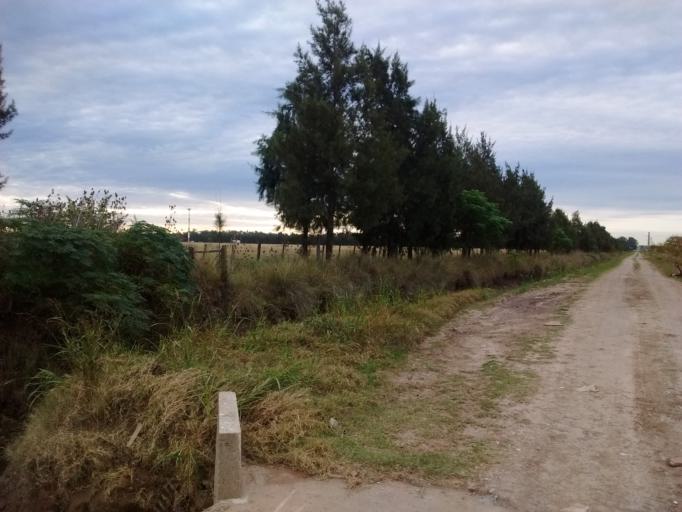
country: AR
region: Santa Fe
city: Funes
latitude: -32.9590
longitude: -60.8192
